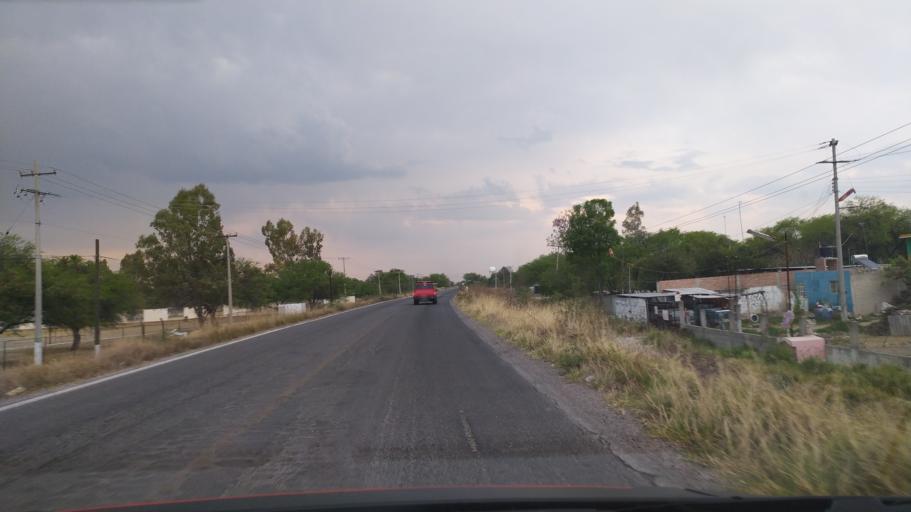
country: MX
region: Guanajuato
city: Ciudad Manuel Doblado
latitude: 20.8108
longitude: -101.9045
